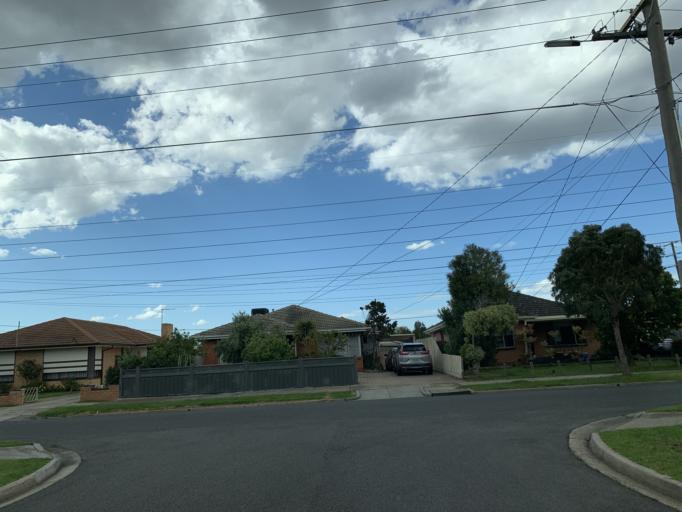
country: AU
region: Victoria
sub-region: Moonee Valley
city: Keilor East
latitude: -37.7423
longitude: 144.8613
